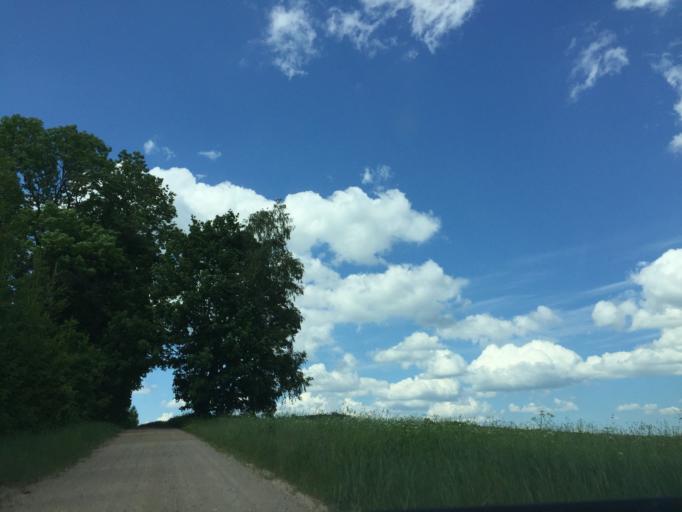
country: LV
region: Priekuli
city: Priekuli
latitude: 57.2350
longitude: 25.4232
